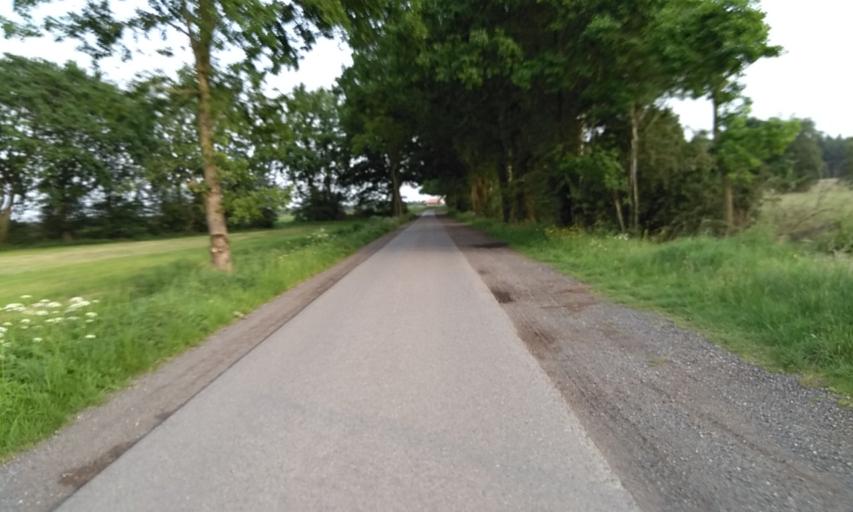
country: DE
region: Lower Saxony
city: Bargstedt
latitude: 53.4919
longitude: 9.4620
